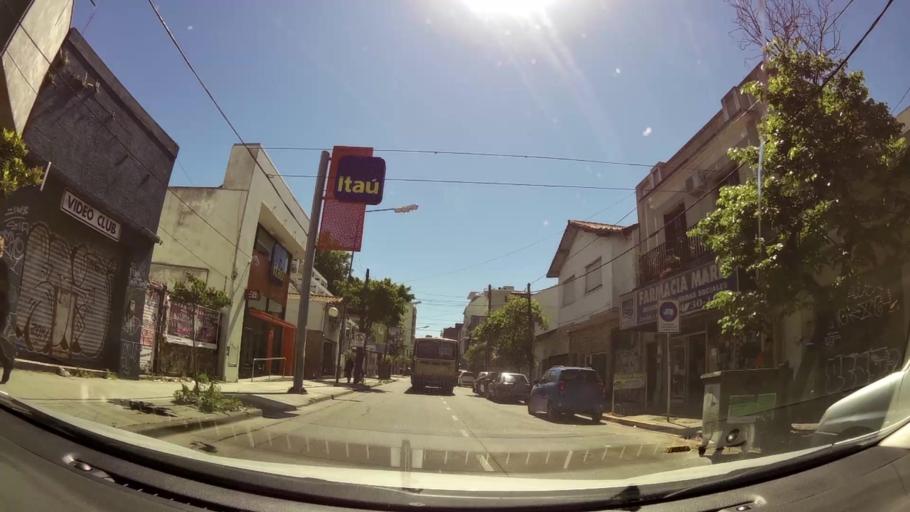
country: AR
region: Buenos Aires
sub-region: Partido de Vicente Lopez
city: Olivos
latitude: -34.5325
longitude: -58.5013
